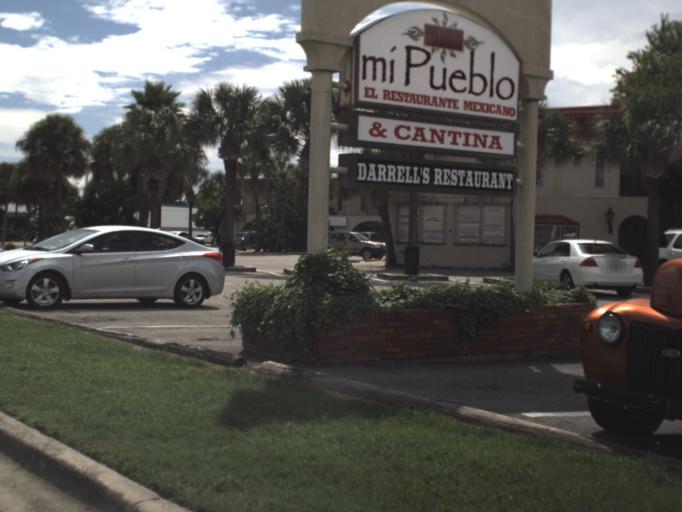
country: US
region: Florida
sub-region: Sarasota County
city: Venice
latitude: 27.0935
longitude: -82.4337
